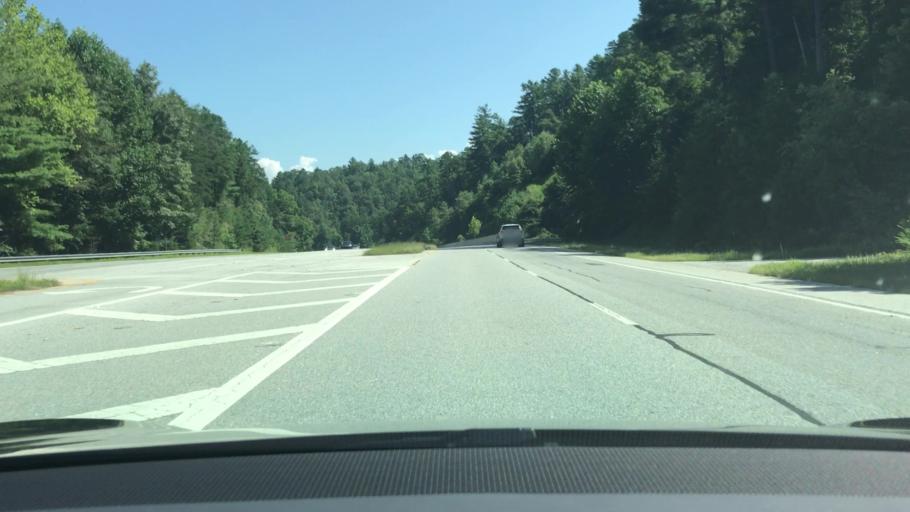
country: US
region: Georgia
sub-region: Rabun County
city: Clayton
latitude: 34.7699
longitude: -83.3964
